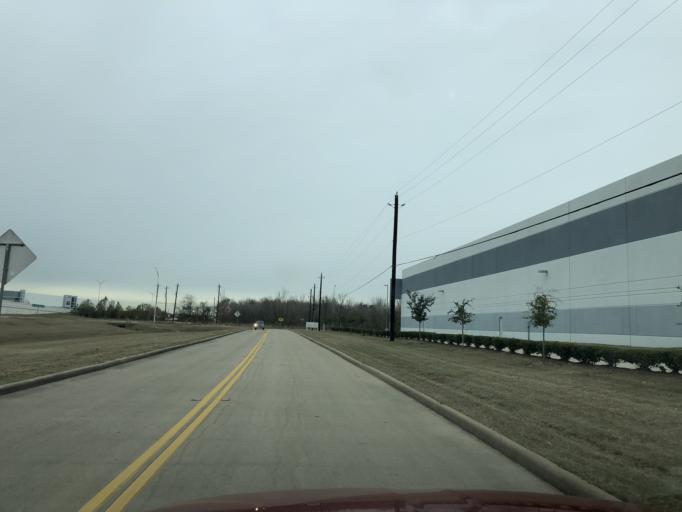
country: US
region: Texas
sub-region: Fort Bend County
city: Missouri City
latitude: 29.6284
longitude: -95.5188
